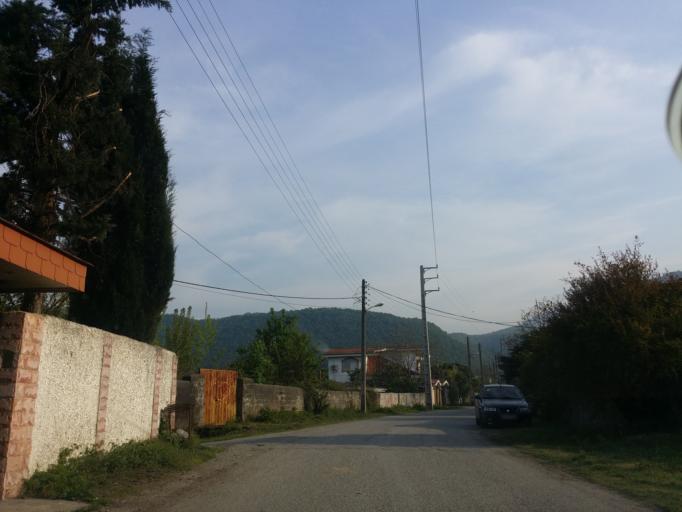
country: IR
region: Mazandaran
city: Chalus
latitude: 36.6579
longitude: 51.3676
